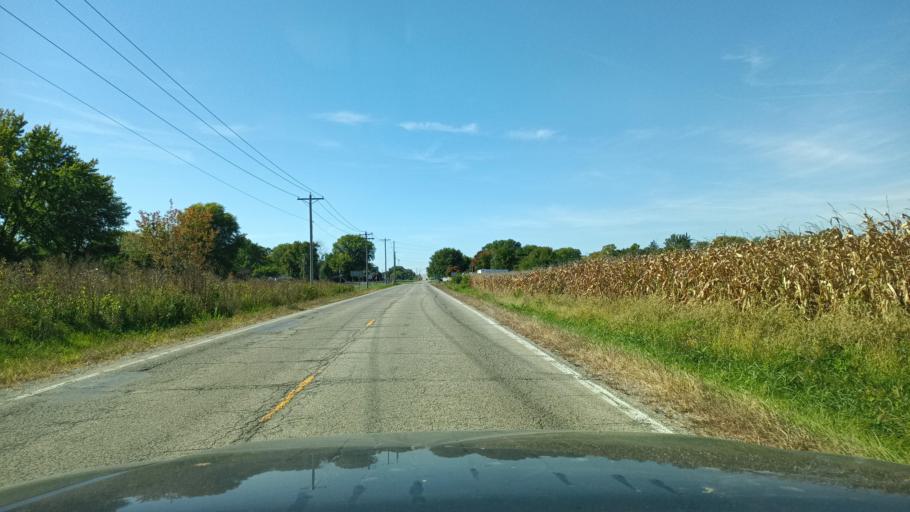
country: US
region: Illinois
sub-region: Champaign County
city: Mahomet
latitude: 40.2115
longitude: -88.4982
